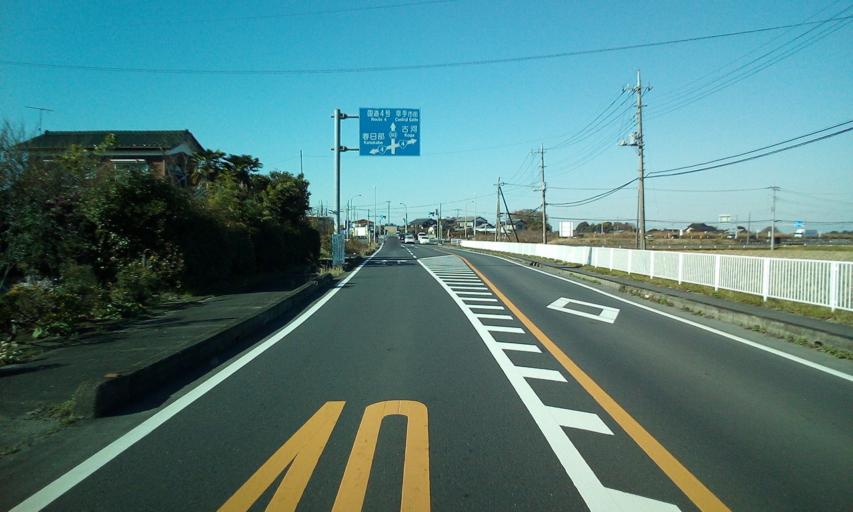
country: JP
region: Saitama
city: Satte
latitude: 36.0524
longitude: 139.7736
